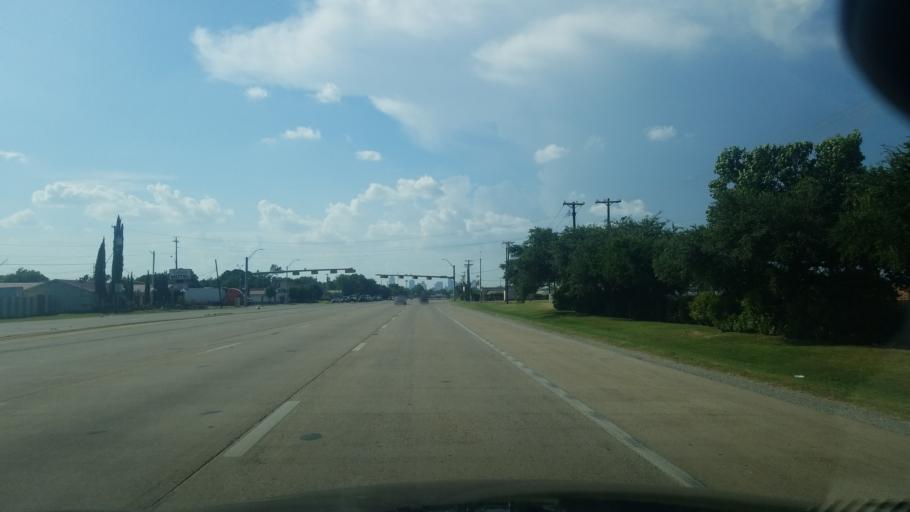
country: US
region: Texas
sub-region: Dallas County
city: Hutchins
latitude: 32.7144
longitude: -96.7544
